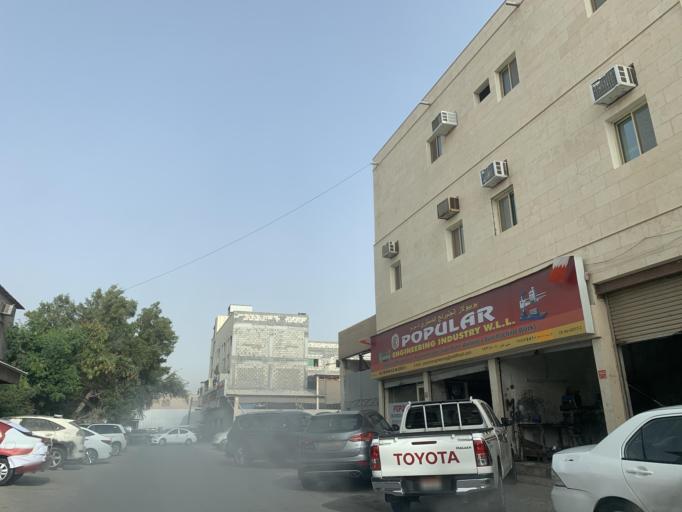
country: BH
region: Northern
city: Madinat `Isa
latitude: 26.1791
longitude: 50.5309
